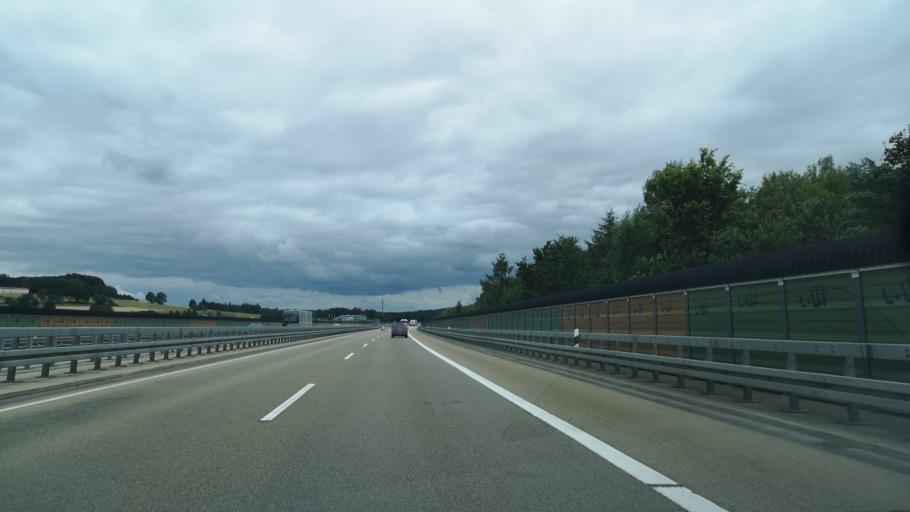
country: DE
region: Bavaria
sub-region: Regierungsbezirk Unterfranken
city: Motten
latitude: 50.4065
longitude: 9.7321
